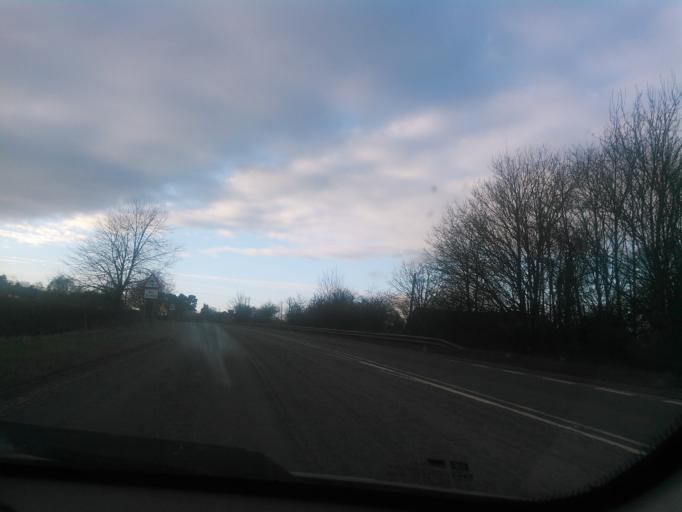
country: GB
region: England
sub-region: Shropshire
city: Market Drayton
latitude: 52.8399
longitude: -2.4627
